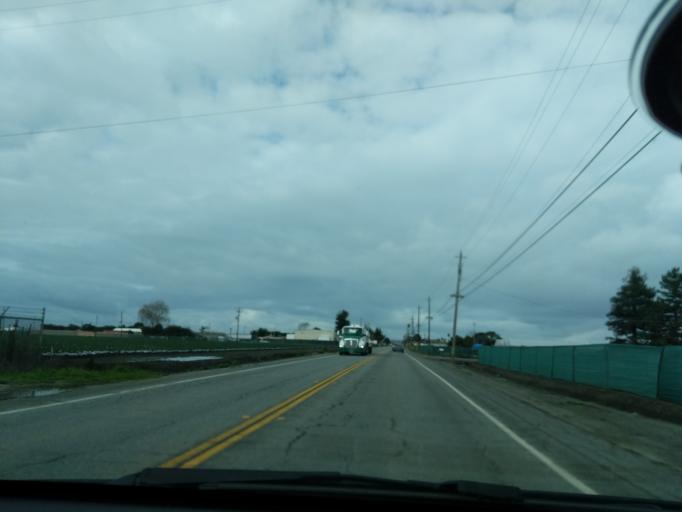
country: US
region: California
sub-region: Monterey County
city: Pajaro
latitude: 36.9043
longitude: -121.7337
